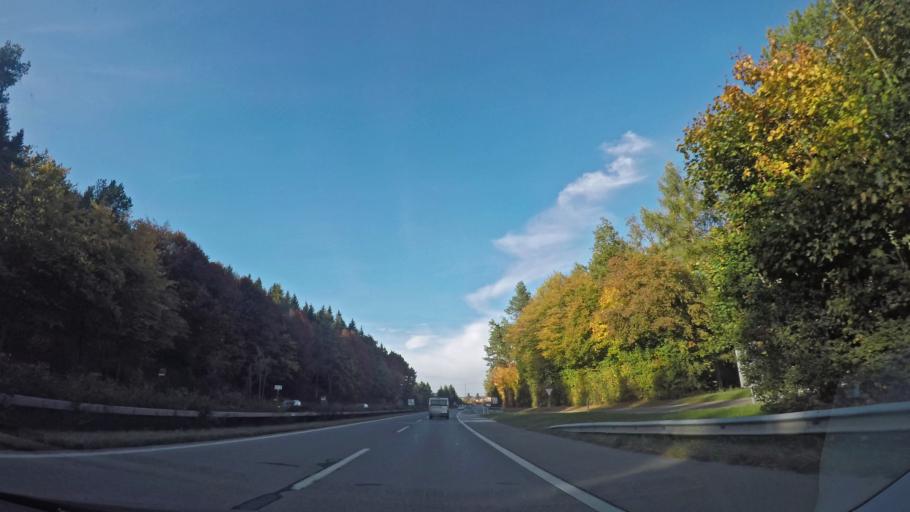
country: CH
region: Bern
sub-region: Thun District
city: Thun
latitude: 46.7332
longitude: 7.6013
